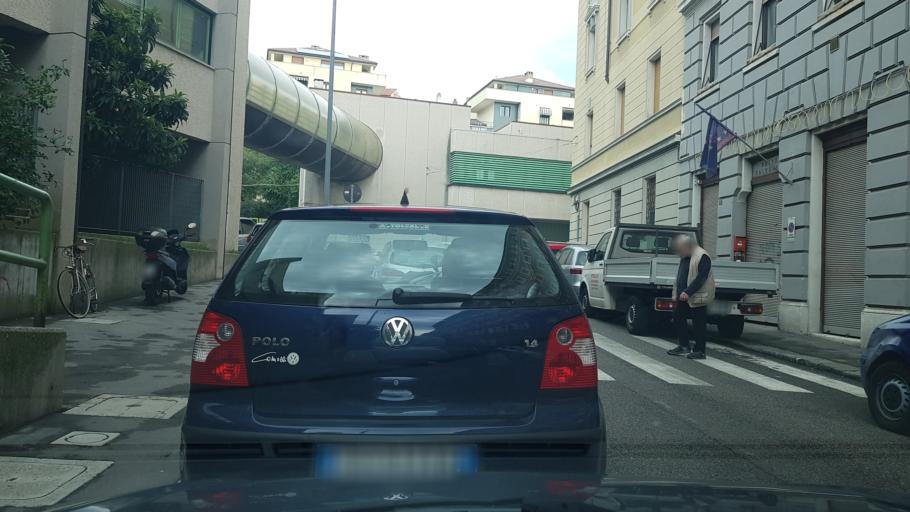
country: IT
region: Friuli Venezia Giulia
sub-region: Provincia di Trieste
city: Trieste
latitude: 45.6554
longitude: 13.7905
